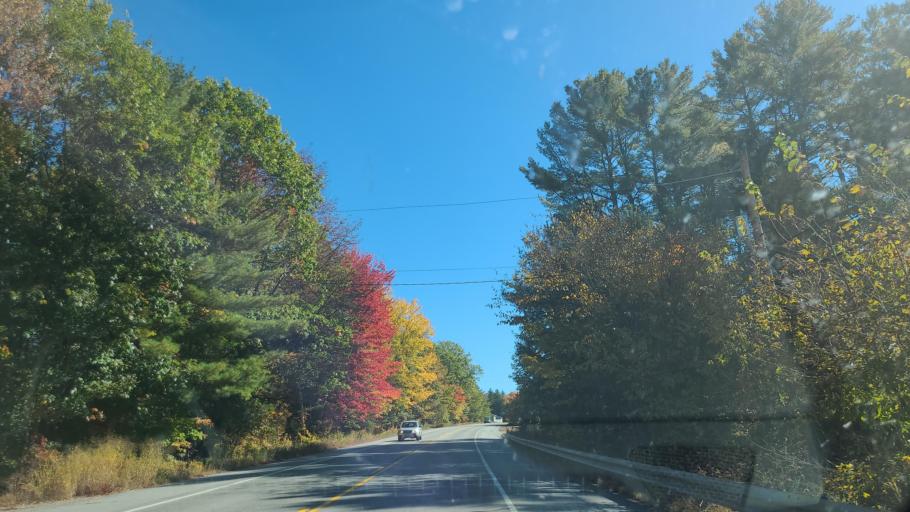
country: US
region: Maine
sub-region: Cumberland County
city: Bridgton
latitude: 44.0690
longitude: -70.7696
